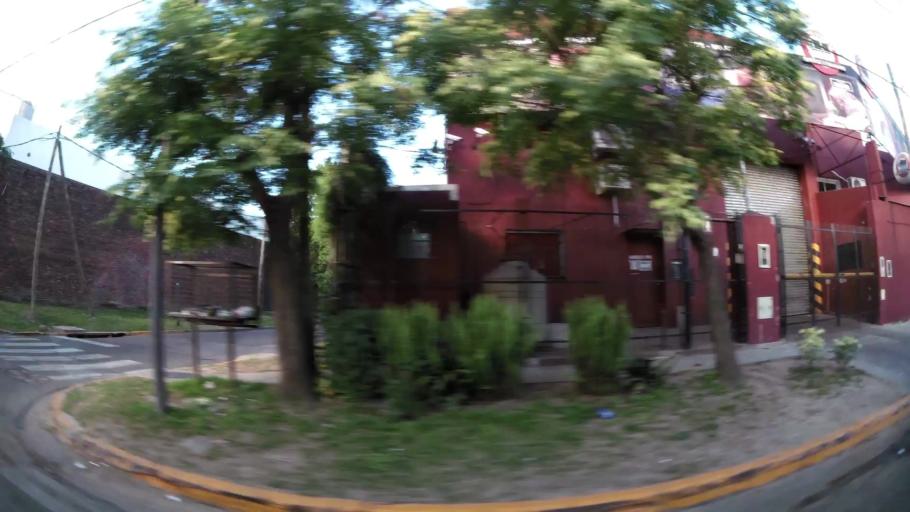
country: AR
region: Buenos Aires
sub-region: Partido de Tigre
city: Tigre
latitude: -34.4494
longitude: -58.5705
